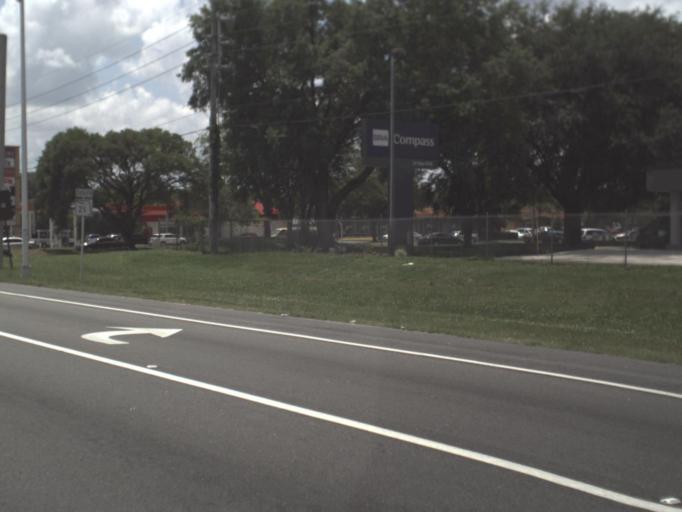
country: US
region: Florida
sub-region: Clay County
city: Bellair-Meadowbrook Terrace
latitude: 30.1946
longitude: -81.7396
